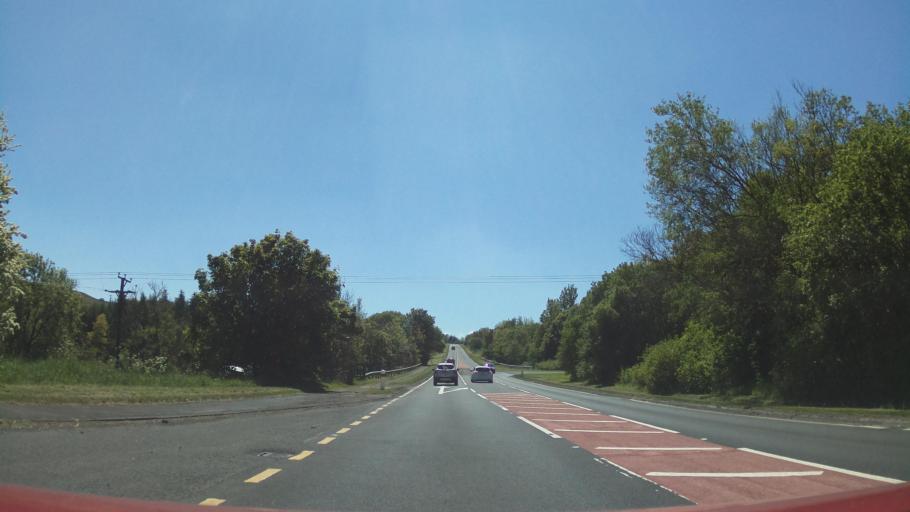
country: GB
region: Scotland
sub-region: The Scottish Borders
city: Selkirk
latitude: 55.4936
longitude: -2.8353
